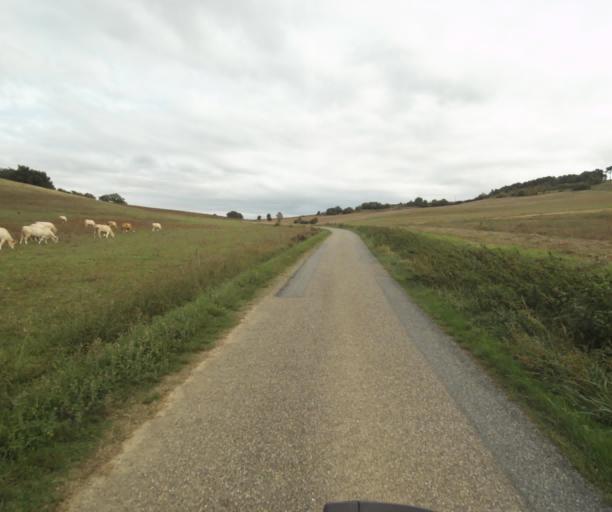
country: FR
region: Midi-Pyrenees
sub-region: Departement du Tarn-et-Garonne
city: Beaumont-de-Lomagne
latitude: 43.8282
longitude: 1.0715
